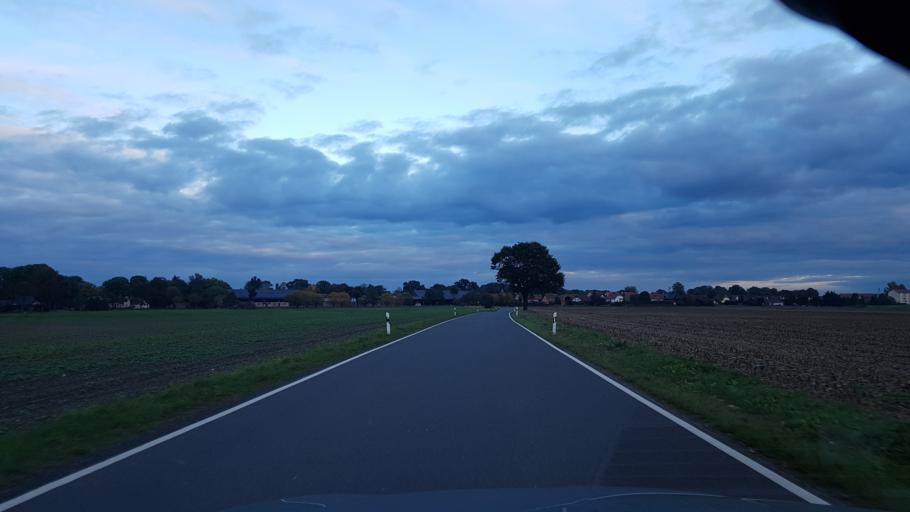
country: DE
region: Saxony
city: Ebersbach
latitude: 51.2792
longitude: 13.6160
